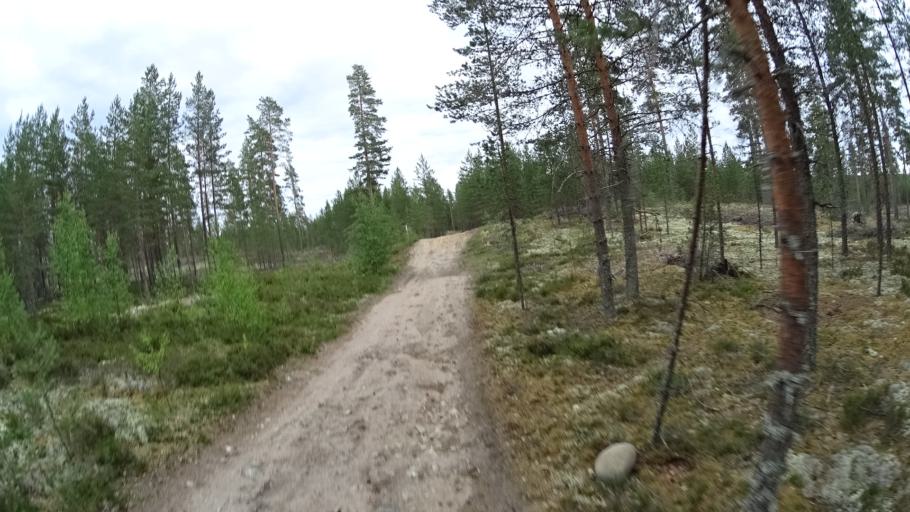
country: FI
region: Satakunta
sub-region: Pohjois-Satakunta
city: Jaemijaervi
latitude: 61.7610
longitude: 22.7780
